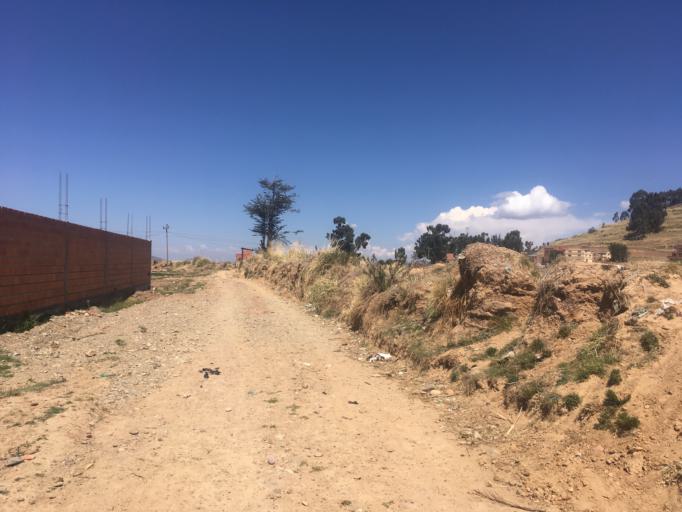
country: BO
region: La Paz
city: Huatajata
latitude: -16.1906
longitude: -68.7470
